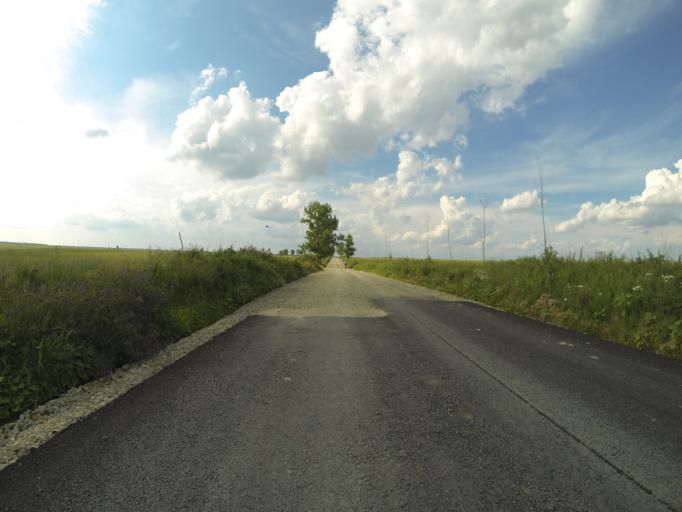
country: RO
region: Dolj
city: Satu Nou Calopar
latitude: 44.1398
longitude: 23.7947
